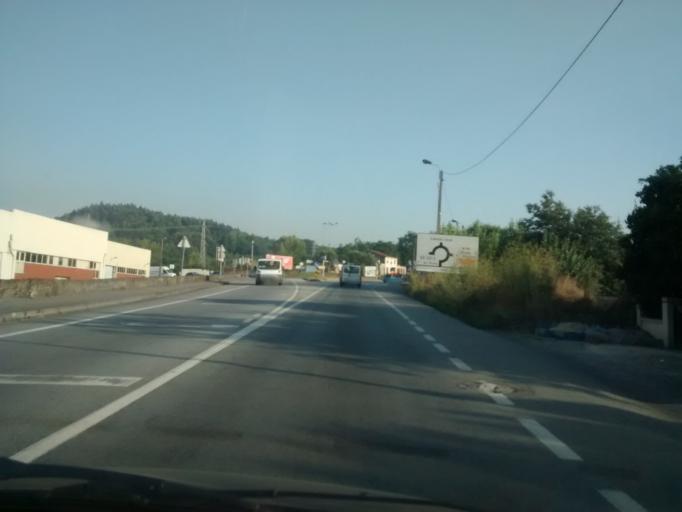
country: PT
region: Braga
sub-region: Braga
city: Braga
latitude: 41.5731
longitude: -8.4239
